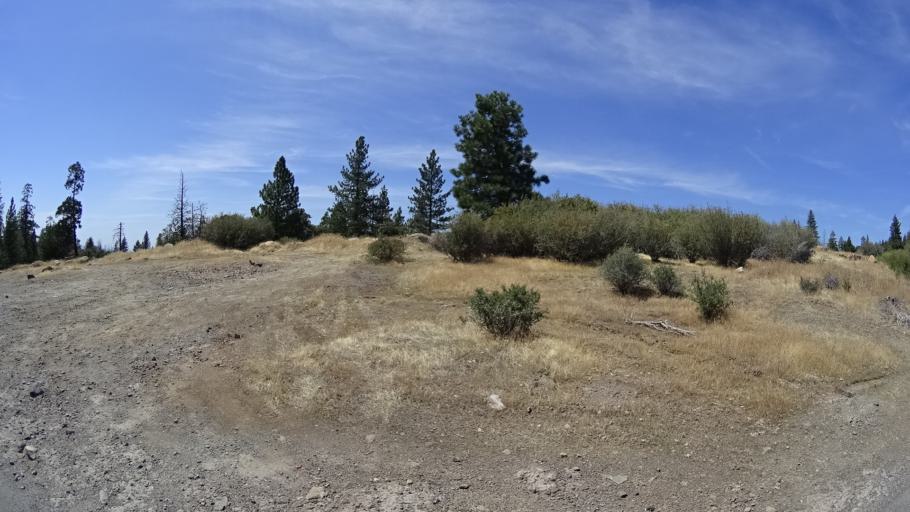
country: US
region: California
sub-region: Calaveras County
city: Forest Meadows
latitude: 38.1970
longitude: -120.3997
